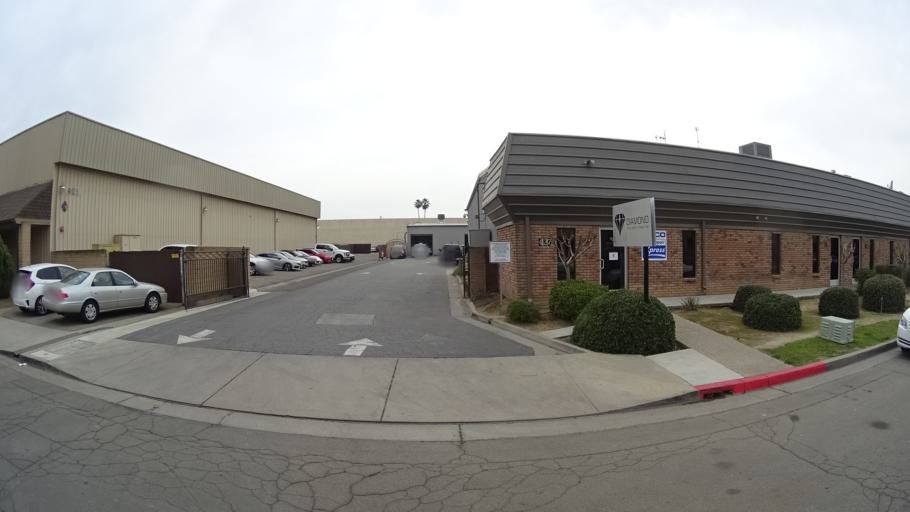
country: US
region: California
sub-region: Fresno County
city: Clovis
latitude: 36.8460
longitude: -119.7996
